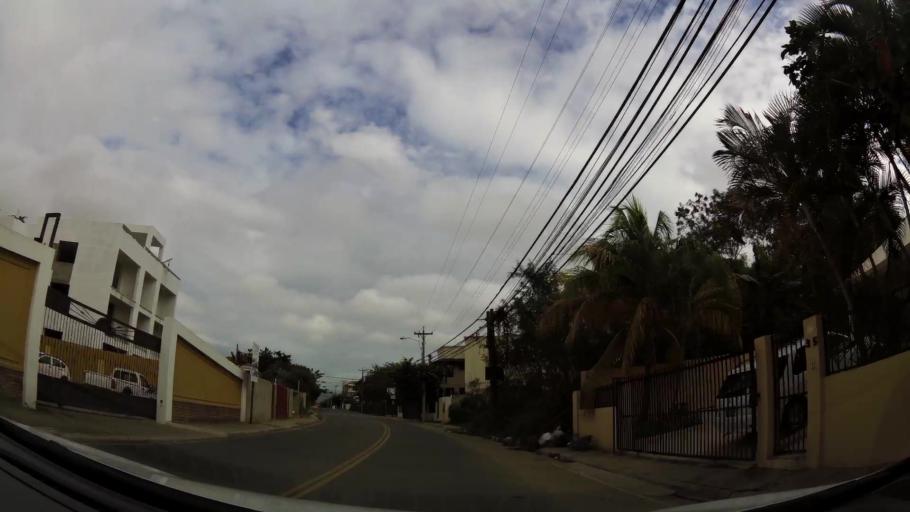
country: DO
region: Santiago
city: Santiago de los Caballeros
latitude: 19.4635
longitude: -70.6571
